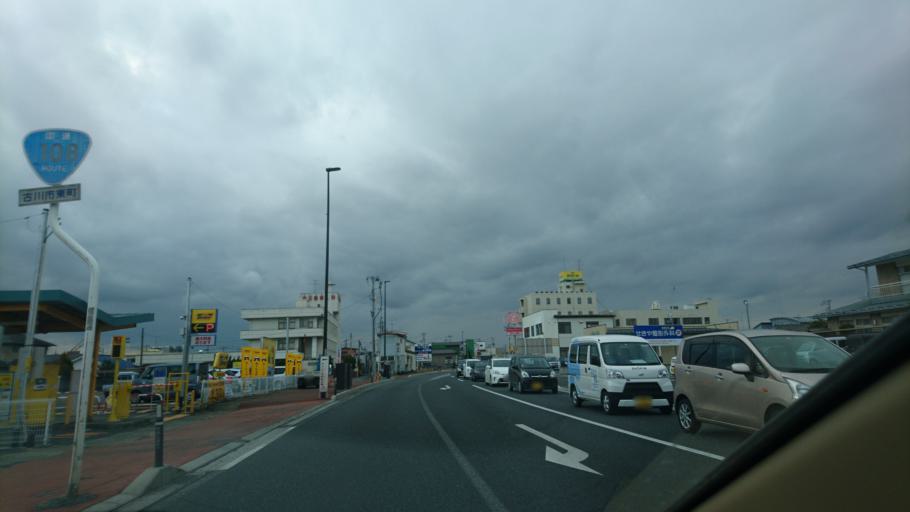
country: JP
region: Miyagi
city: Furukawa
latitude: 38.5764
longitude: 140.9653
